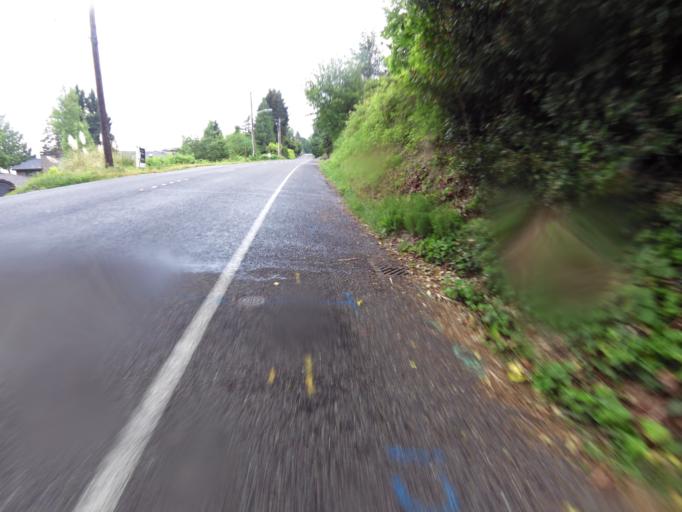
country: US
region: Washington
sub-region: King County
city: Mercer Island
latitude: 47.5327
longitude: -122.2175
